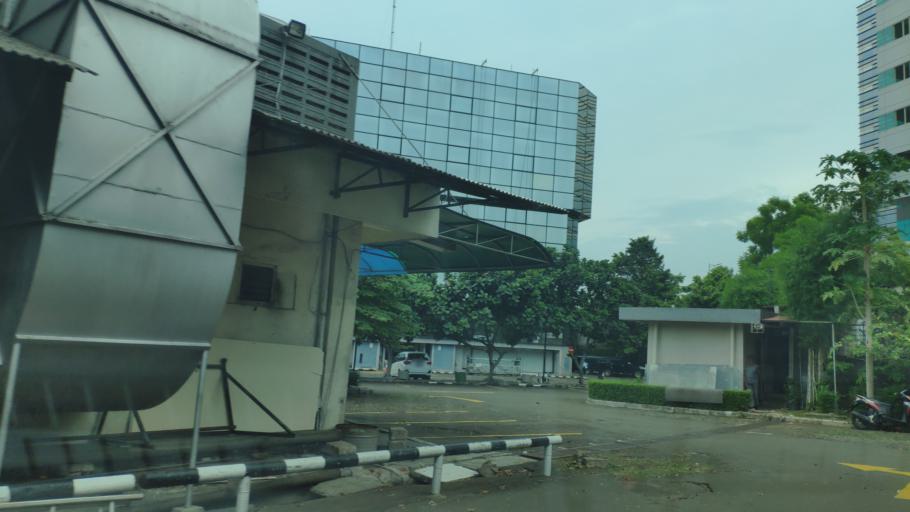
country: ID
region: Jakarta Raya
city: Jakarta
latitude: -6.1915
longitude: 106.7985
